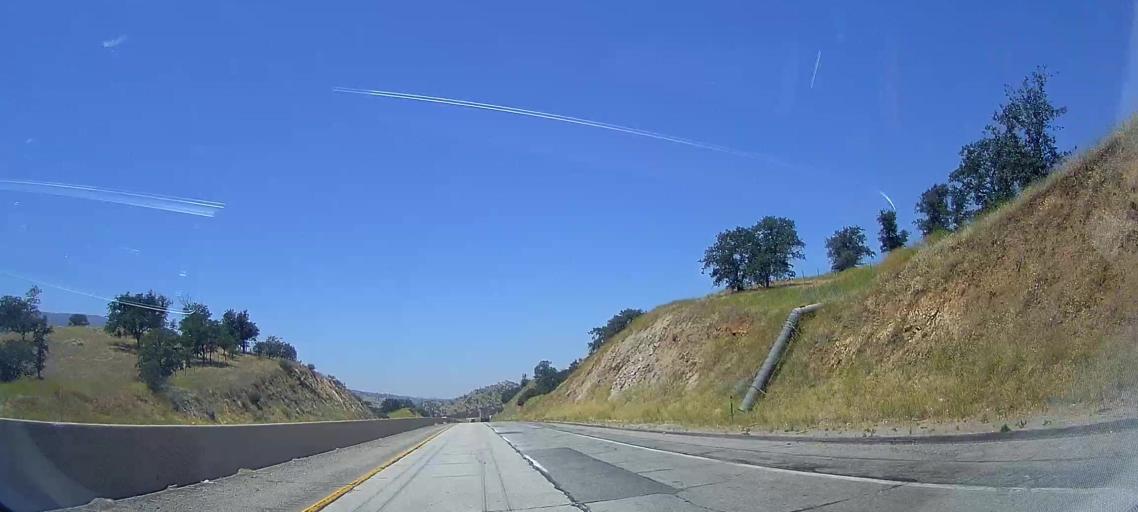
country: US
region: California
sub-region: Kern County
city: Golden Hills
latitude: 35.1941
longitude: -118.5125
